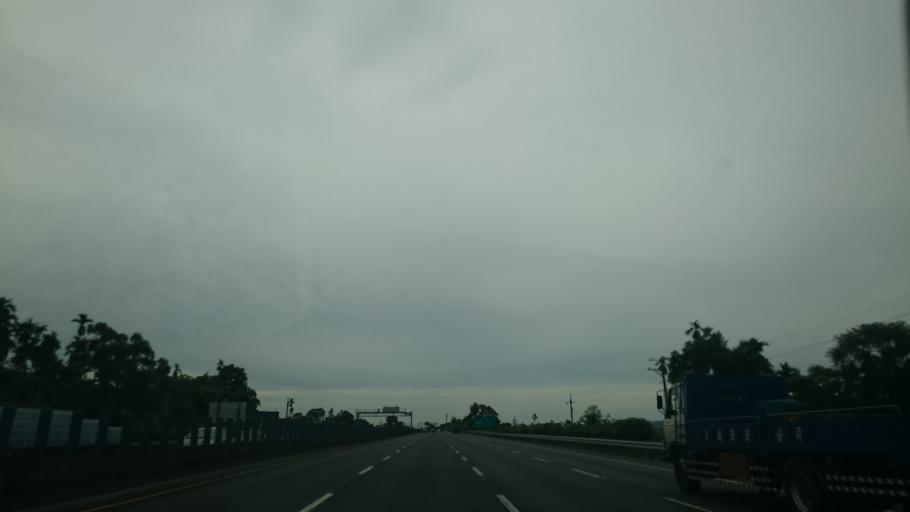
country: TW
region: Taiwan
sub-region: Nantou
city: Nantou
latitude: 23.8697
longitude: 120.7049
